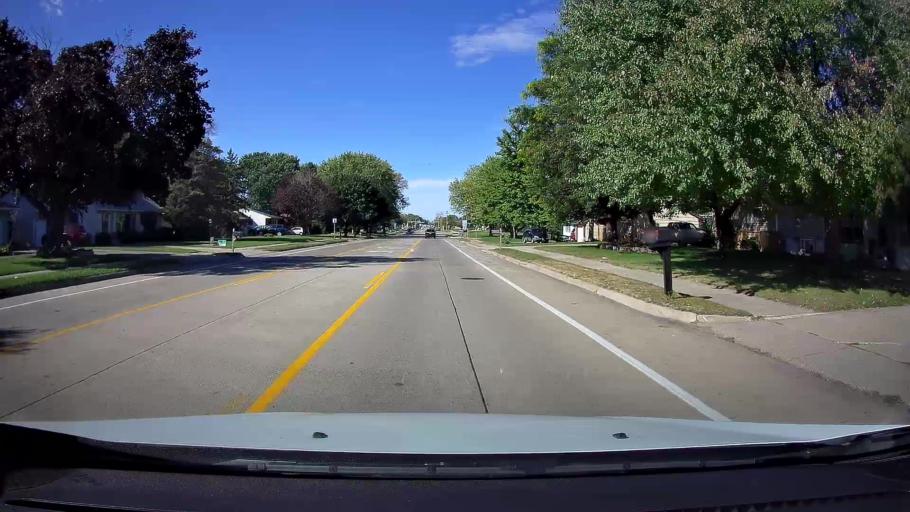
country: US
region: Minnesota
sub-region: Ramsey County
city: Roseville
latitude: 45.0063
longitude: -93.1583
